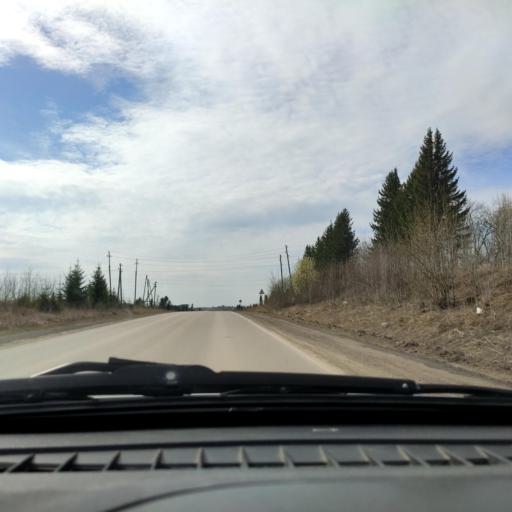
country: RU
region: Perm
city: Lobanovo
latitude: 57.8598
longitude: 56.2958
